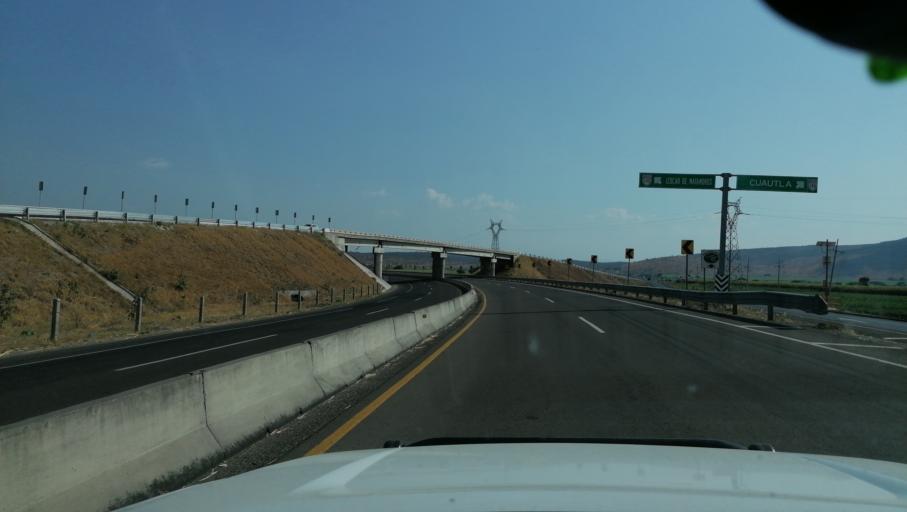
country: MX
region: Puebla
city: San Cristobal Tepeojuma
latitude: 18.7152
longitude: -98.4540
